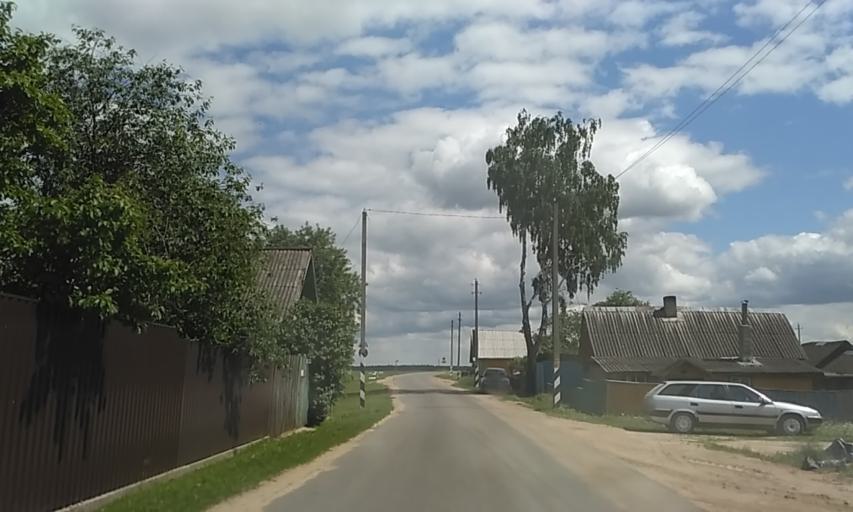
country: BY
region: Minsk
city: Krupki
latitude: 54.3484
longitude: 29.1334
